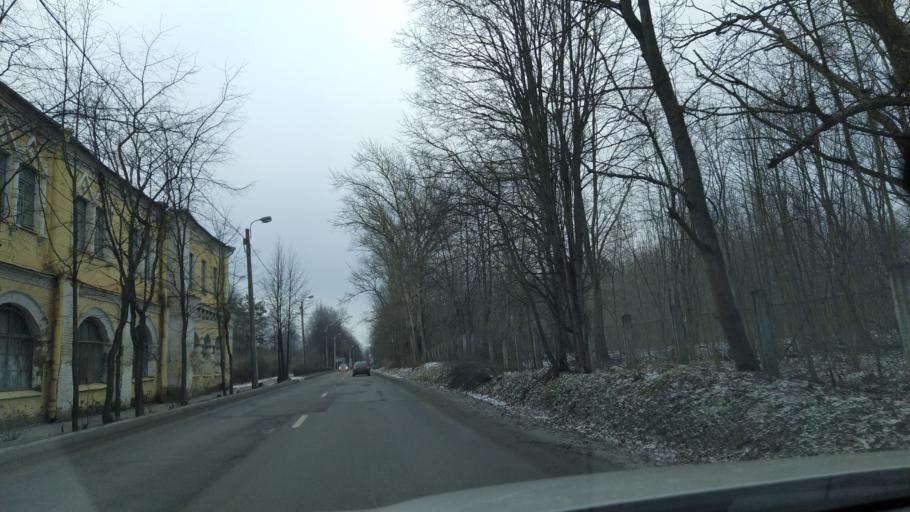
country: RU
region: St.-Petersburg
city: Pushkin
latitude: 59.7274
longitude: 30.3912
